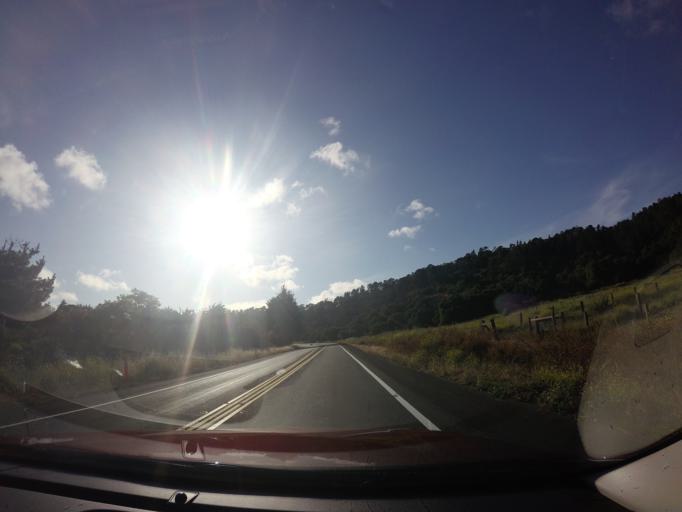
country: US
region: California
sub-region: Monterey County
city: Del Rey Oaks
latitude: 36.5396
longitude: -121.8634
